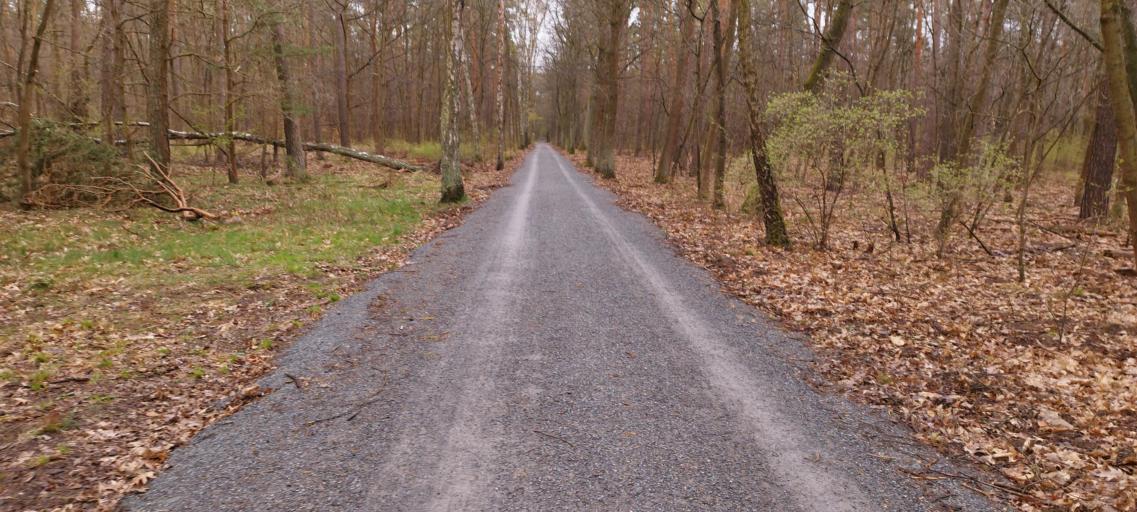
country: DE
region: Berlin
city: Rahnsdorf
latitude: 52.4564
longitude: 13.6894
